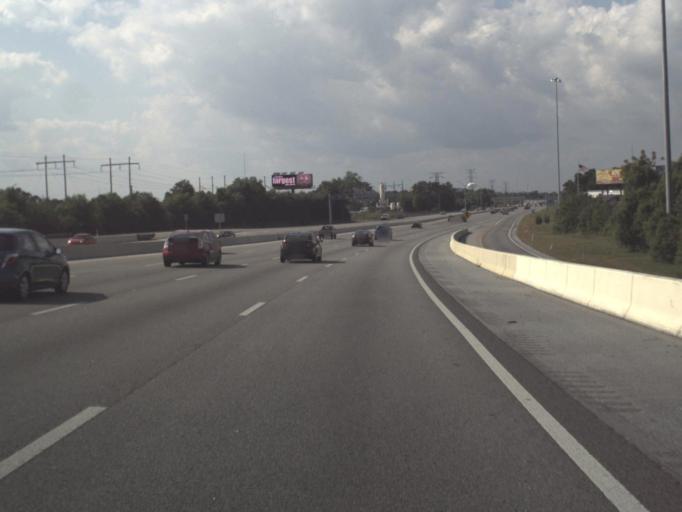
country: US
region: Florida
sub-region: Escambia County
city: Goulding
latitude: 30.4542
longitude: -87.2230
